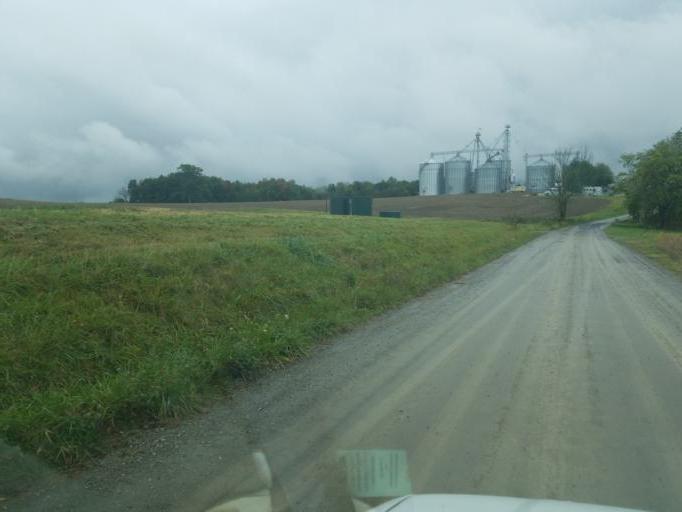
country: US
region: Ohio
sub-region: Holmes County
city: Millersburg
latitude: 40.5795
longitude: -81.9945
